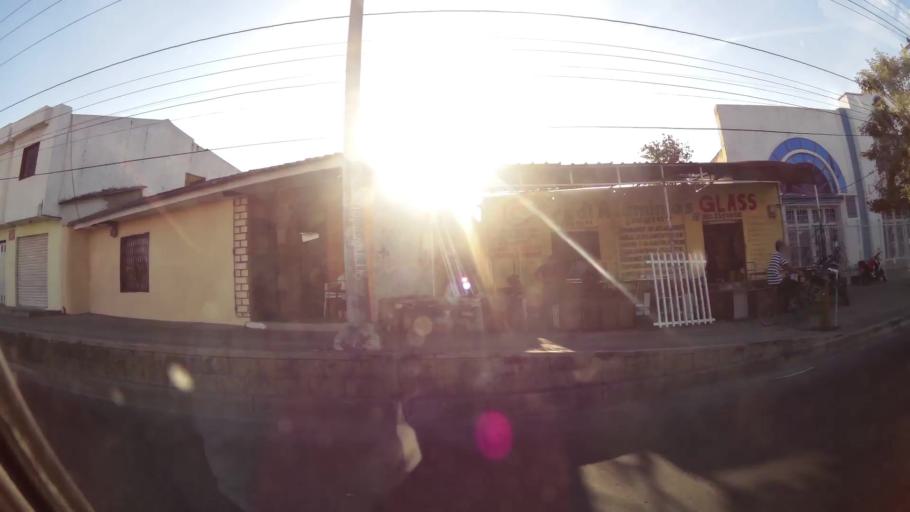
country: CO
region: Atlantico
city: Barranquilla
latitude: 10.9407
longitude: -74.7996
